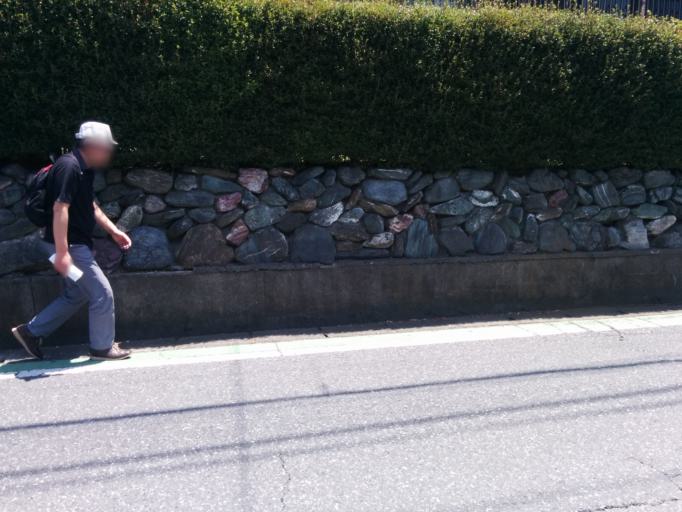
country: JP
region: Tokyo
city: Higashimurayama-shi
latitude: 35.7677
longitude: 139.4674
